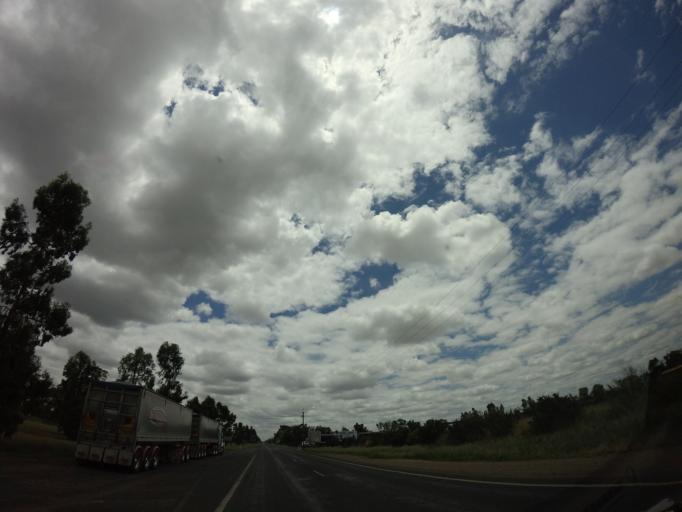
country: AU
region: Queensland
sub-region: Goondiwindi
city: Goondiwindi
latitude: -28.5229
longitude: 150.2875
